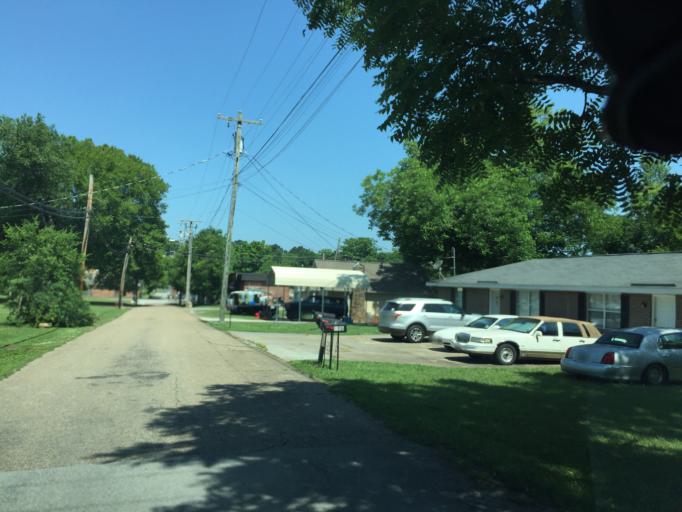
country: US
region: Tennessee
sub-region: Hamilton County
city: Collegedale
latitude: 35.0730
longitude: -85.0611
